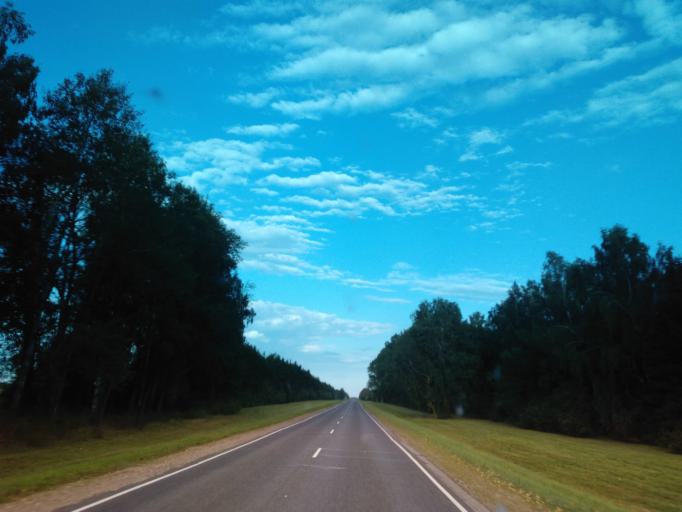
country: BY
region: Minsk
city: Uzda
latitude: 53.4390
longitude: 27.3073
